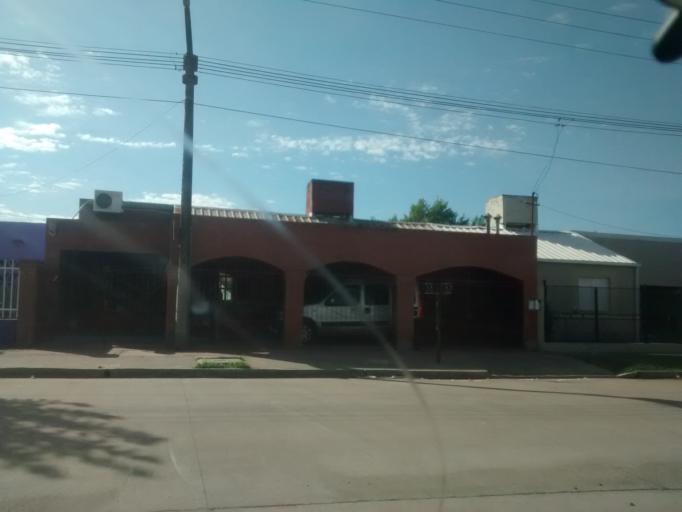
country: AR
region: Chaco
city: Puerto Tirol
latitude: -27.3719
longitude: -59.0981
